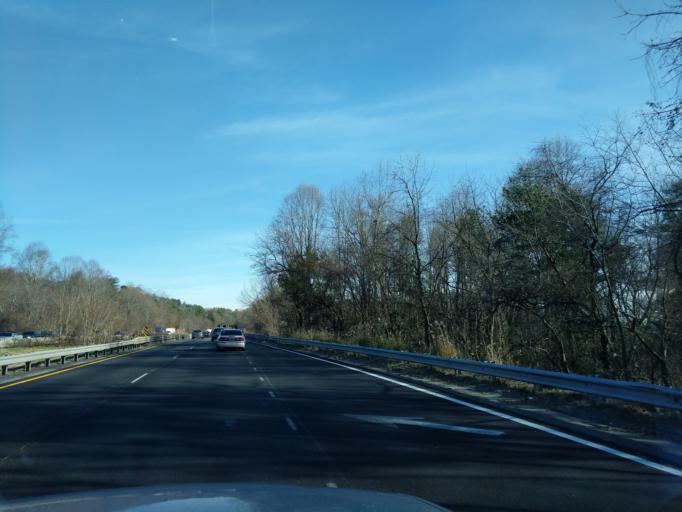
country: US
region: North Carolina
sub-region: Henderson County
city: Mountain Home
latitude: 35.3979
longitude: -82.5044
